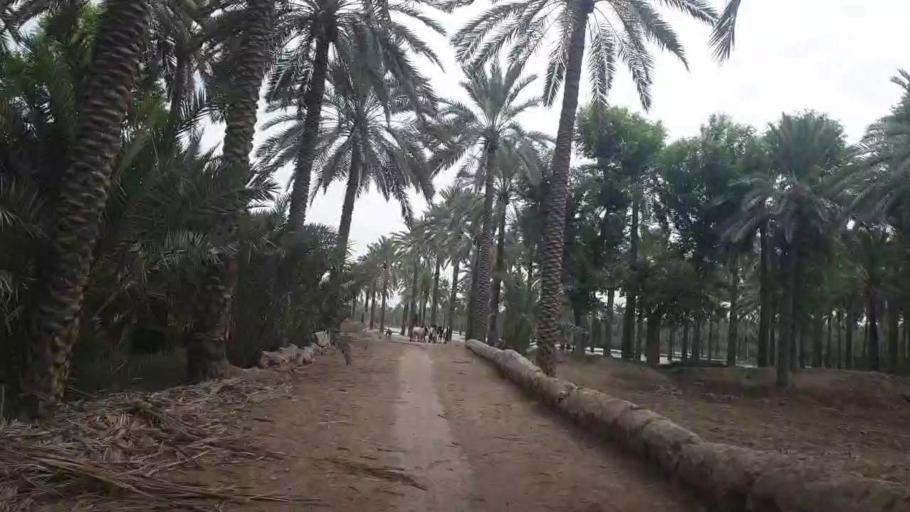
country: PK
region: Sindh
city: Khairpur
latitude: 27.5859
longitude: 68.7495
